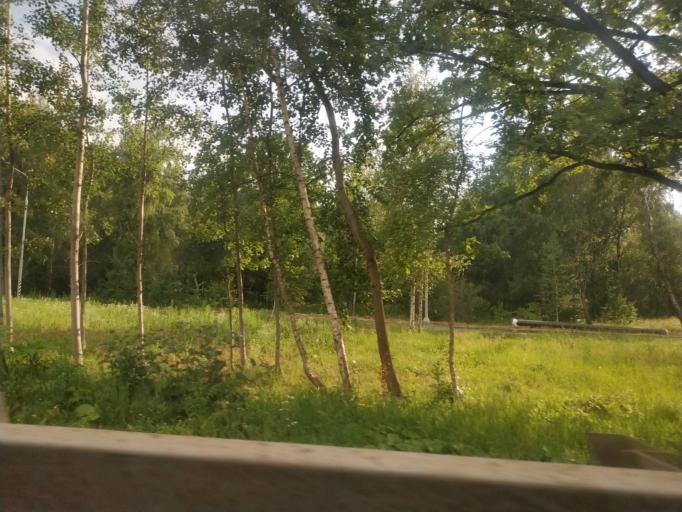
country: RU
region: Moskovskaya
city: Kommunarka
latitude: 55.5852
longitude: 37.4594
